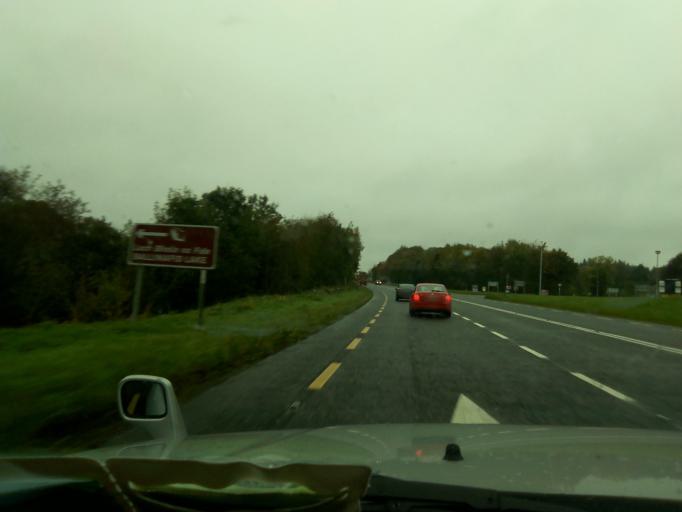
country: IE
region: Leinster
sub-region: An Iarmhi
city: An Muileann gCearr
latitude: 53.5959
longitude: -7.3809
